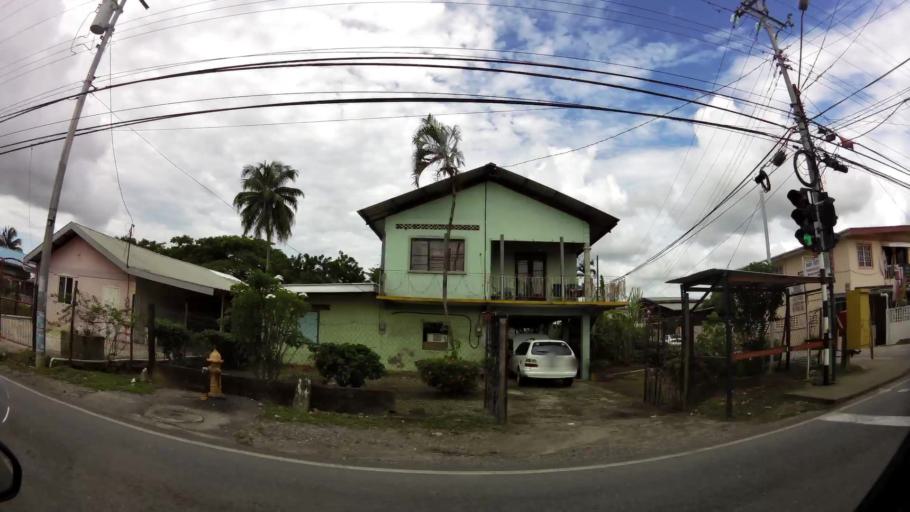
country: TT
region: Chaguanas
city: Chaguanas
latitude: 10.4956
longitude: -61.4083
